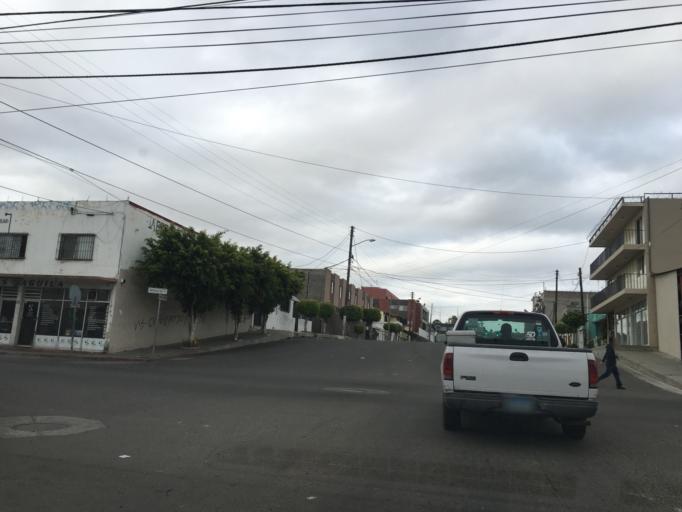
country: MX
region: Baja California
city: Tijuana
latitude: 32.5360
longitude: -117.0474
